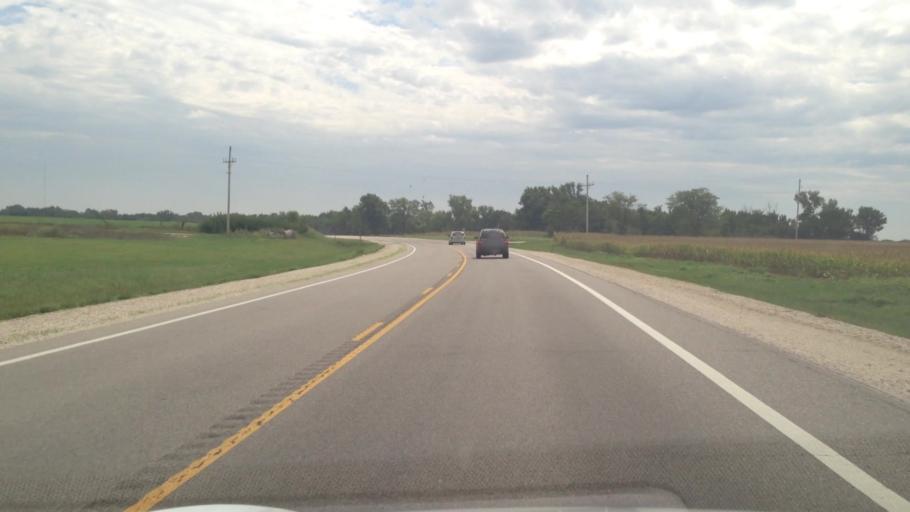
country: US
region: Kansas
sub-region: Allen County
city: Iola
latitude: 37.9167
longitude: -95.1533
